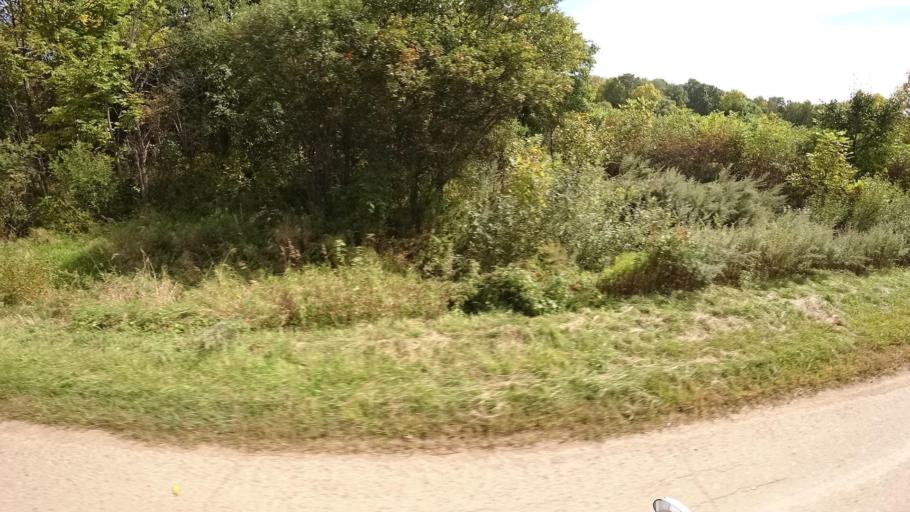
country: RU
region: Primorskiy
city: Yakovlevka
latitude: 44.7476
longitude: 133.6058
